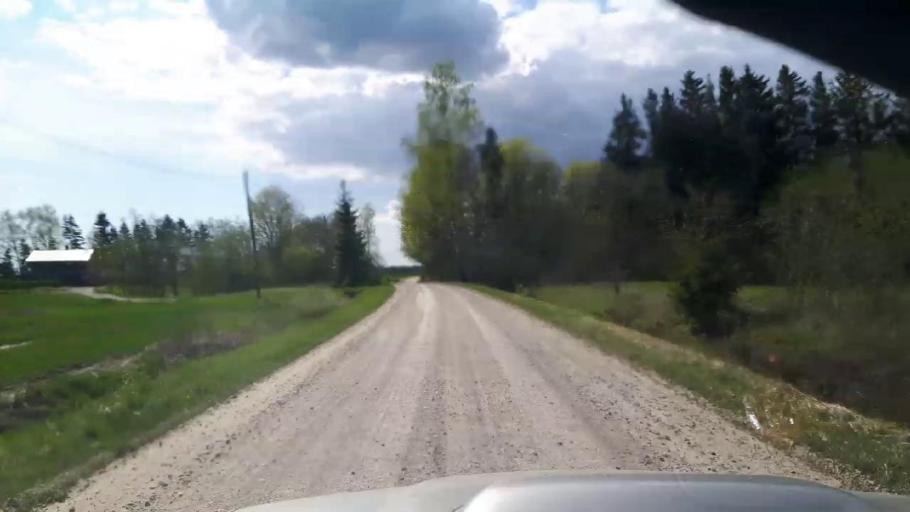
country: EE
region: Paernumaa
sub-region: Sindi linn
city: Sindi
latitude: 58.4198
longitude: 24.7237
